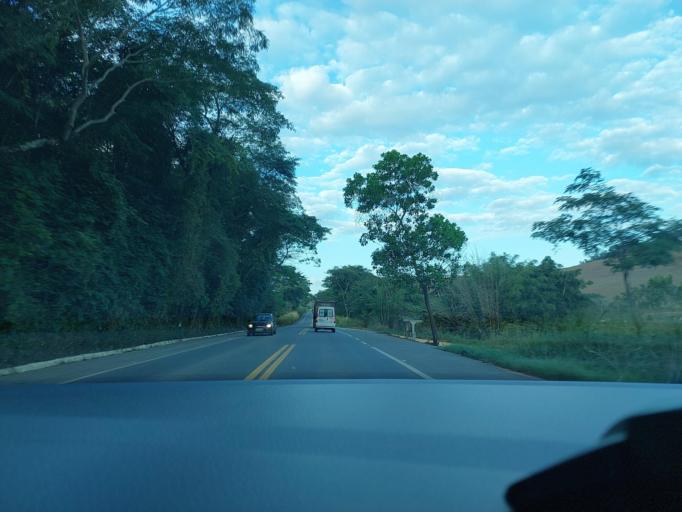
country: BR
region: Minas Gerais
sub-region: Muriae
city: Muriae
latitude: -21.1491
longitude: -42.1592
